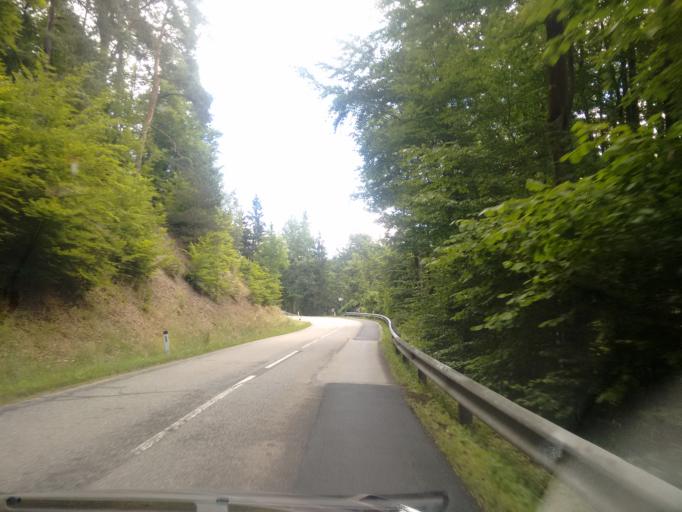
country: AT
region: Upper Austria
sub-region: Politischer Bezirk Urfahr-Umgebung
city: Gramastetten
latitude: 48.3681
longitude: 14.1732
